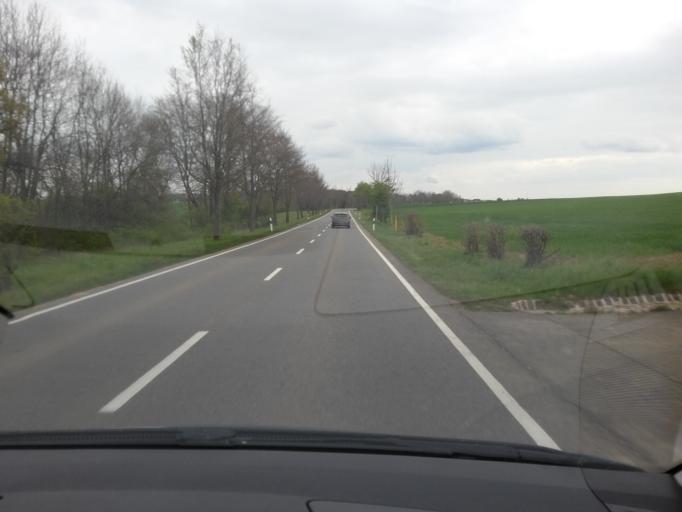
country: LU
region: Luxembourg
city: Schouweiler
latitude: 49.5961
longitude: 5.9552
